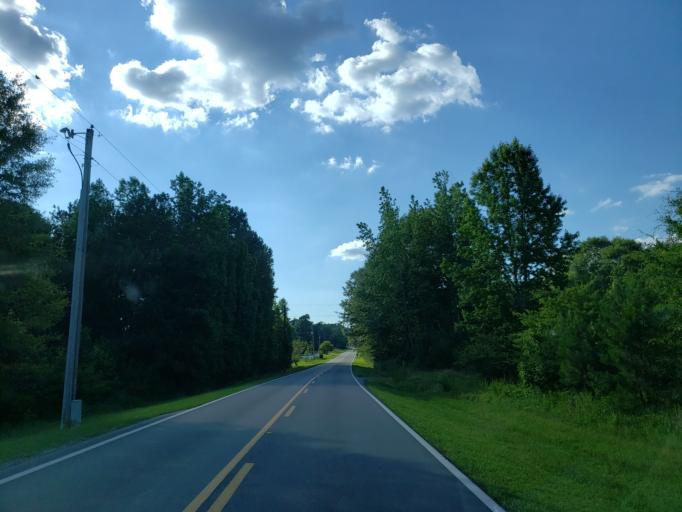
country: US
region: Georgia
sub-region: Haralson County
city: Bremen
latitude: 33.6809
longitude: -85.1278
